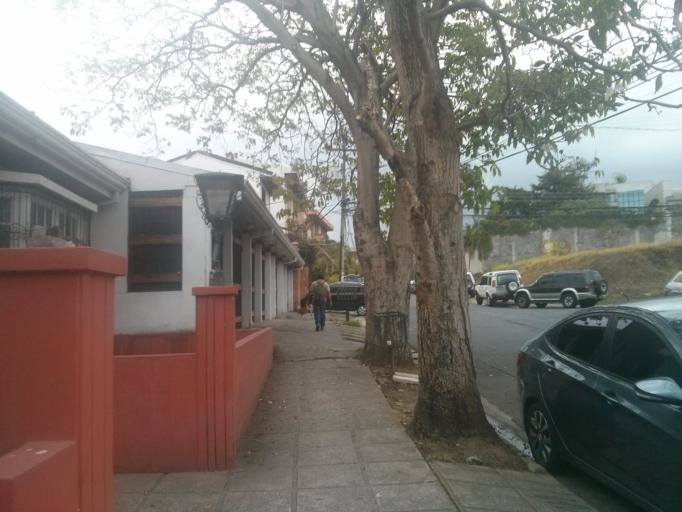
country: CR
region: San Jose
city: San Pedro
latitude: 9.9369
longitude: -84.0565
